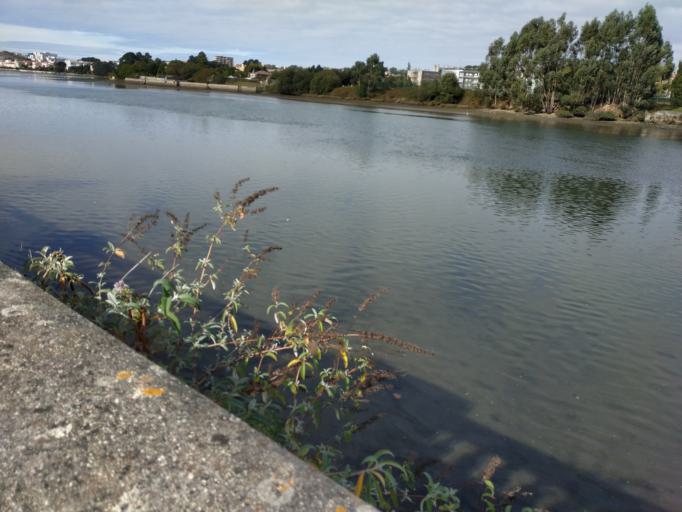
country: ES
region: Galicia
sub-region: Provincia da Coruna
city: Cambre
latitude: 43.3206
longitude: -8.3656
